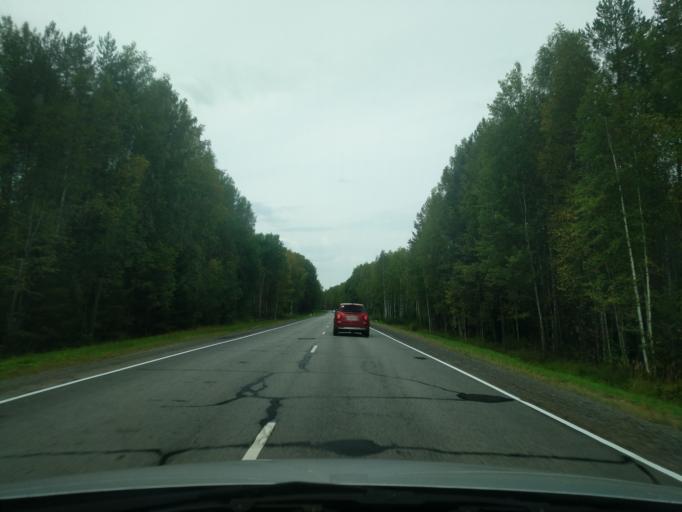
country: RU
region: Kirov
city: Kotel'nich
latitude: 58.2712
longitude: 48.0818
